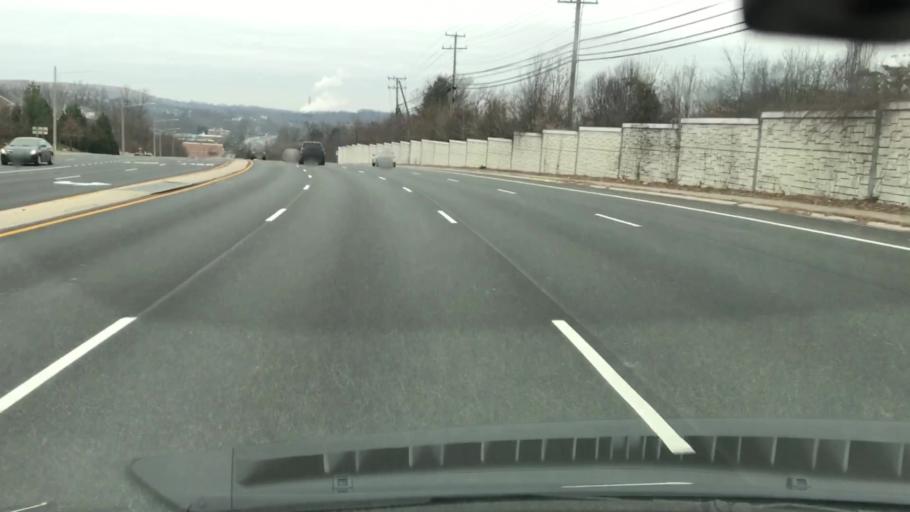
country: US
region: Virginia
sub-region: Fairfax County
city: Lorton
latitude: 38.7084
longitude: -77.1981
